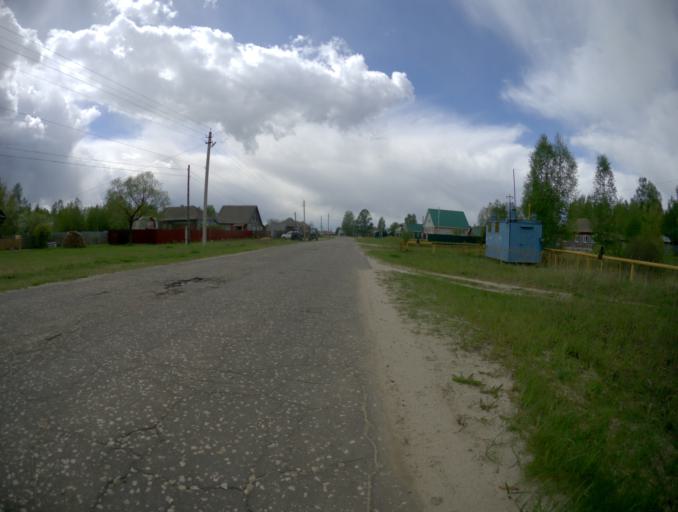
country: RU
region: Vladimir
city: Velikodvorskiy
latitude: 55.2477
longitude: 40.6862
